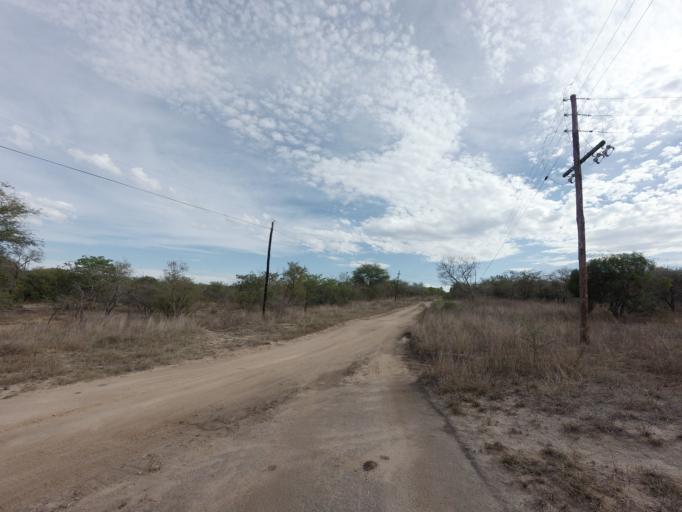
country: ZA
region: Limpopo
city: Thulamahashi
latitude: -24.5245
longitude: 31.1224
